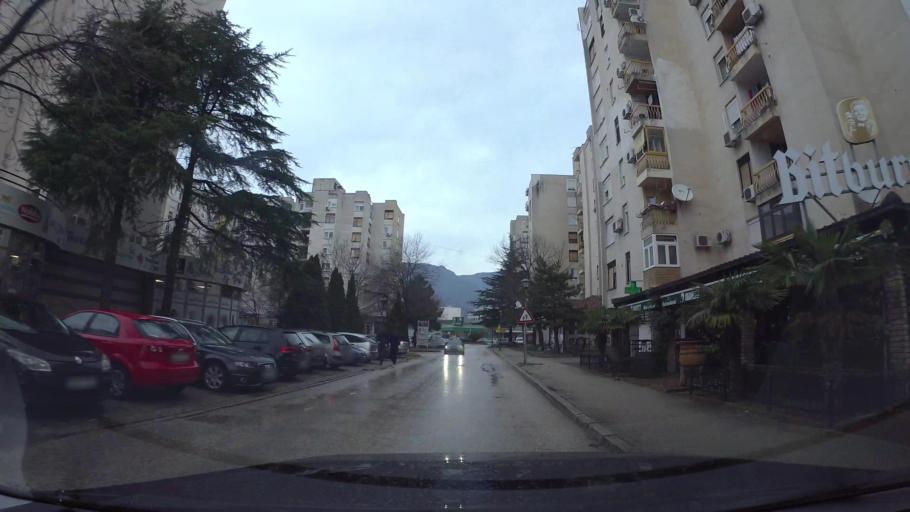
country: BA
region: Federation of Bosnia and Herzegovina
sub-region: Hercegovacko-Bosanski Kanton
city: Mostar
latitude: 43.3513
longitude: 17.8049
